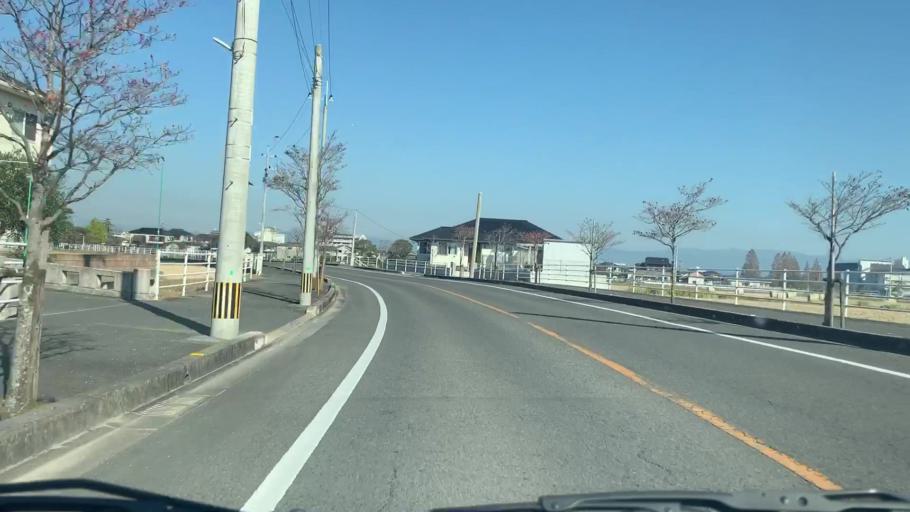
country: JP
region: Saga Prefecture
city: Saga-shi
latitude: 33.2341
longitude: 130.3129
